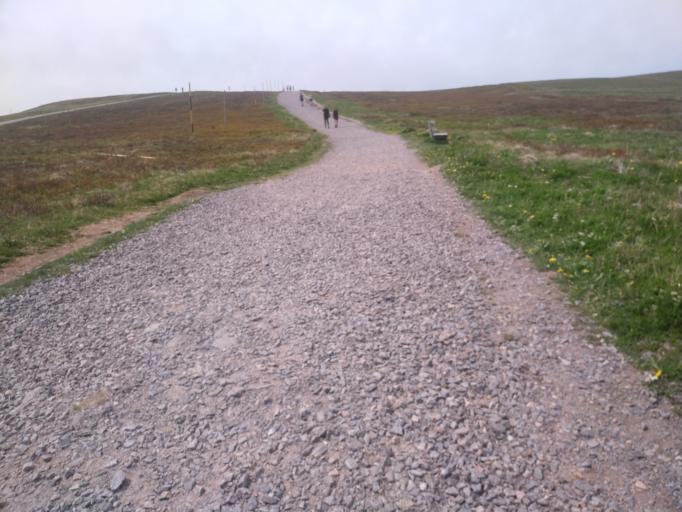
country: DE
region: Baden-Wuerttemberg
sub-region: Freiburg Region
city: Bernau
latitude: 47.8682
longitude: 8.0163
